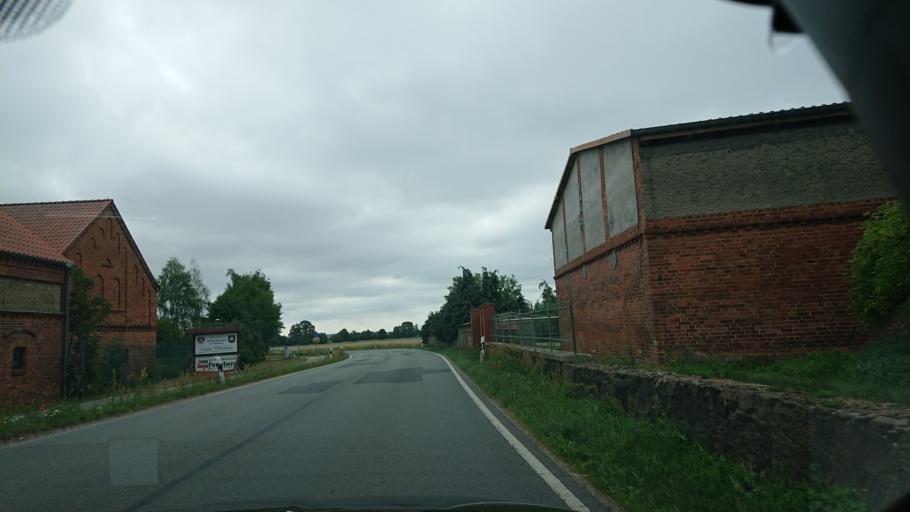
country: DE
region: Brandenburg
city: Perleberg
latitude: 53.0619
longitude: 11.8981
